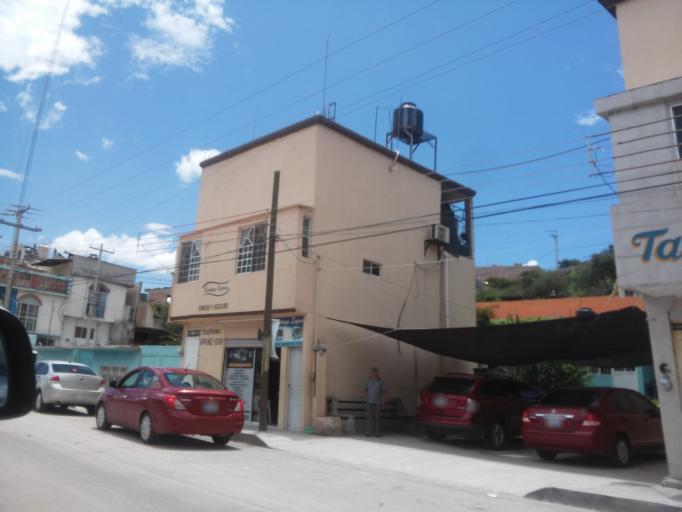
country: MX
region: Durango
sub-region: Santiago Papasquiaro
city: Santiago Papasquiaro
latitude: 25.0491
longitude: -105.4230
